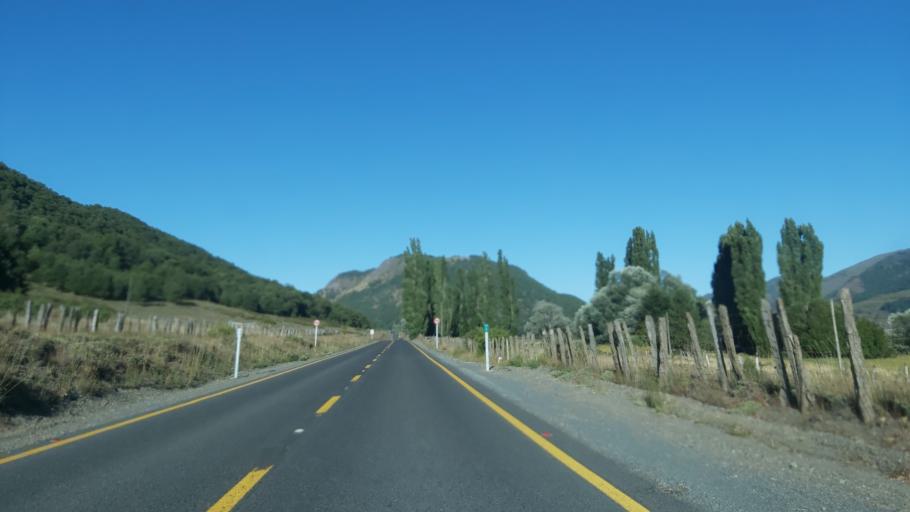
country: AR
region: Neuquen
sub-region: Departamento de Loncopue
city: Loncopue
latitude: -38.4461
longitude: -71.3555
